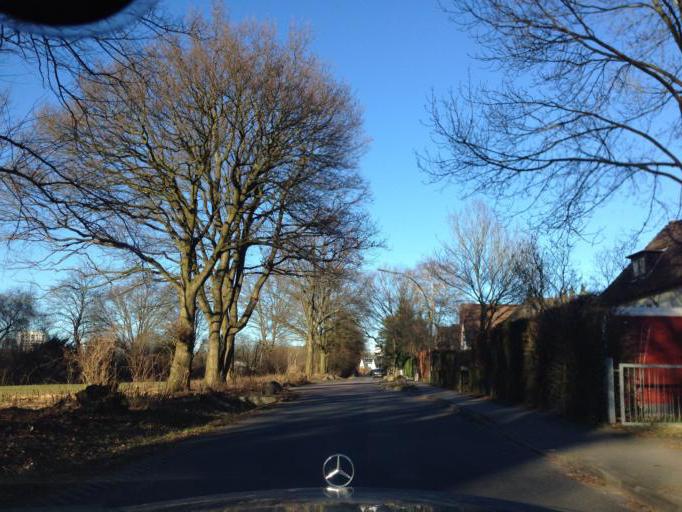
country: DE
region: Hamburg
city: Farmsen-Berne
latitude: 53.6139
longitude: 10.1291
